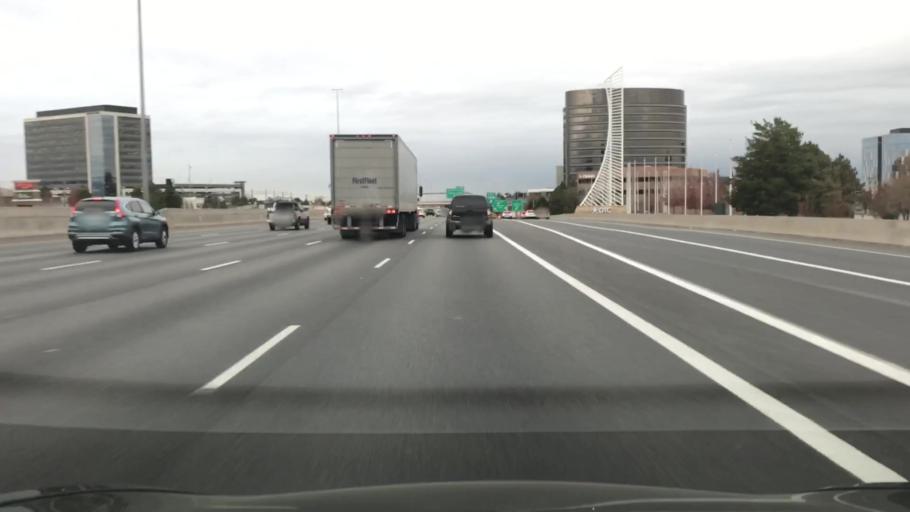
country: US
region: Colorado
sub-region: Arapahoe County
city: Castlewood
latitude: 39.6207
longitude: -104.8995
